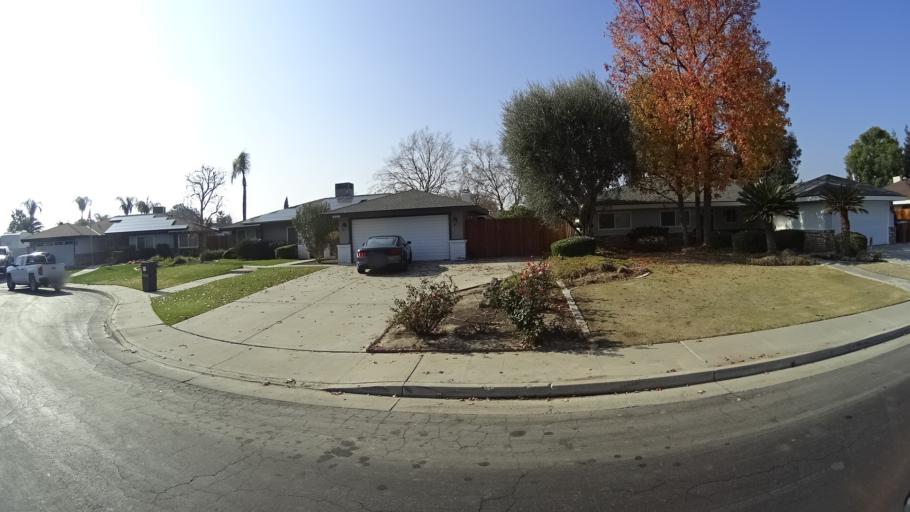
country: US
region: California
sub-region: Kern County
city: Greenacres
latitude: 35.3248
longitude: -119.0807
